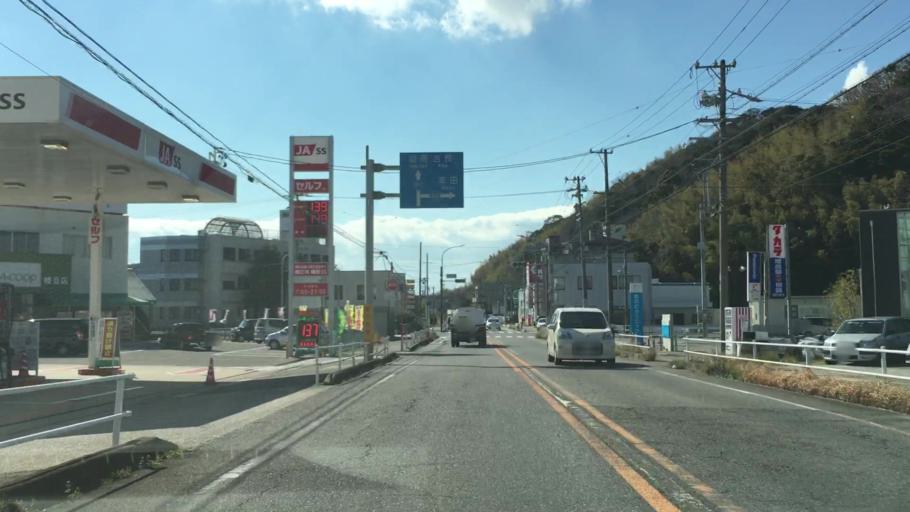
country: JP
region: Aichi
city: Nishio
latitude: 34.7955
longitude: 137.1163
